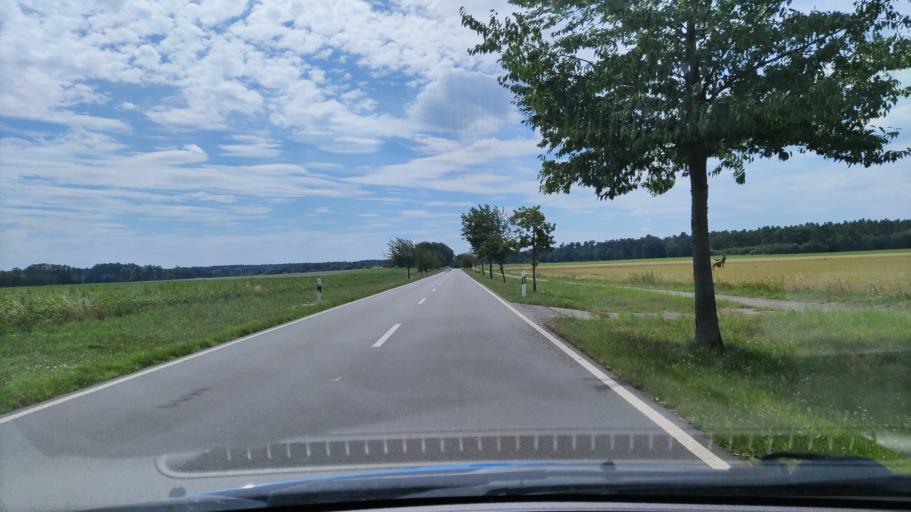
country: DE
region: Lower Saxony
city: Clenze
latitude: 52.9228
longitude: 10.9487
